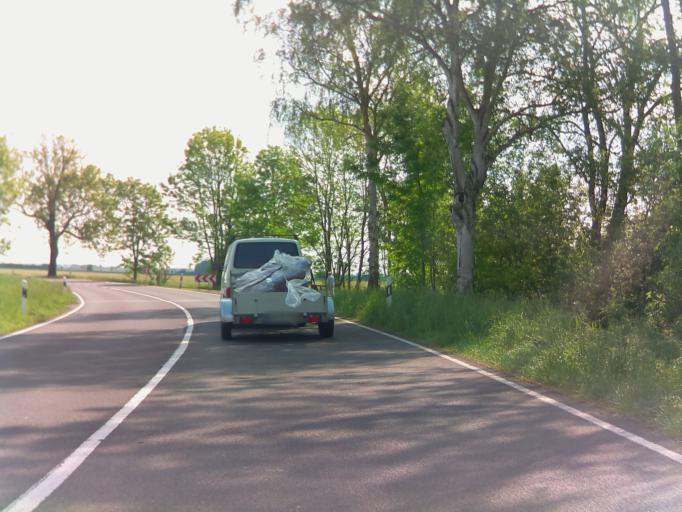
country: DE
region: Saxony-Anhalt
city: Luderitz
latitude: 52.5634
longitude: 11.7615
